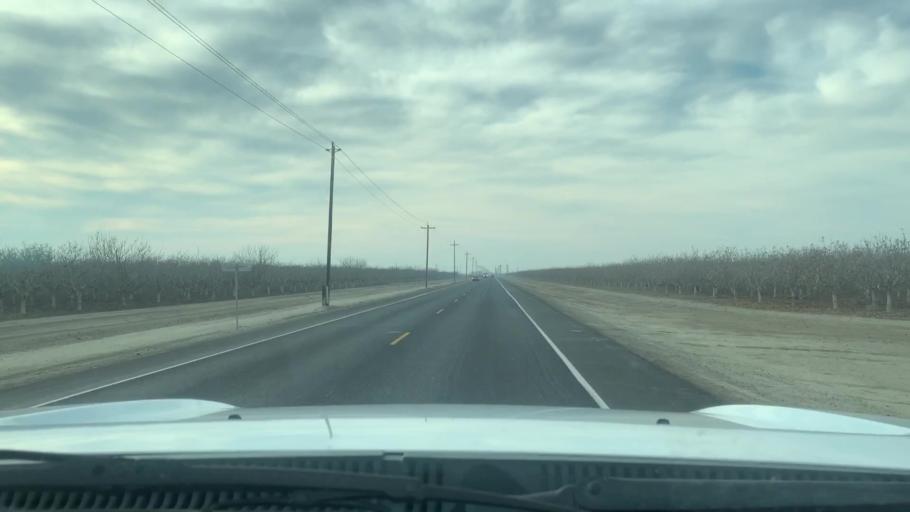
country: US
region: California
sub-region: Kern County
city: Buttonwillow
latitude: 35.4423
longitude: -119.4229
